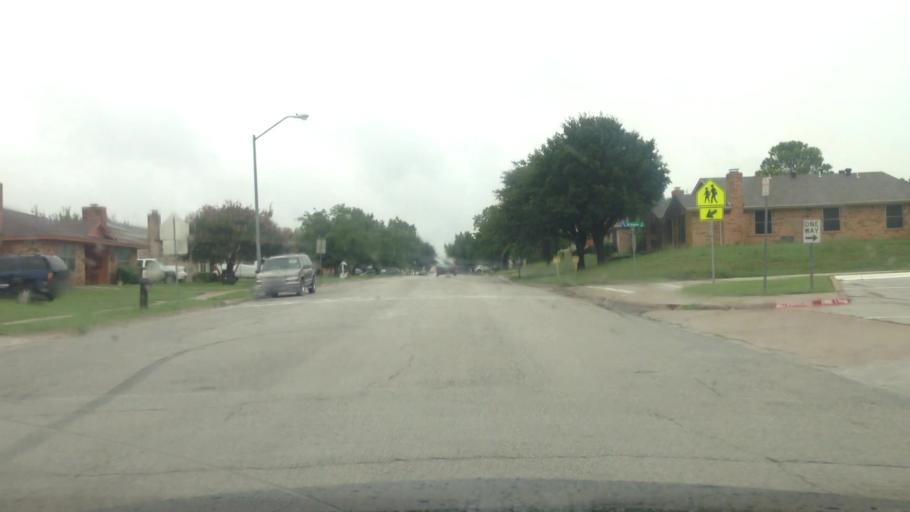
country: US
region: Texas
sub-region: Tarrant County
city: Watauga
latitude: 32.8762
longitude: -97.2330
